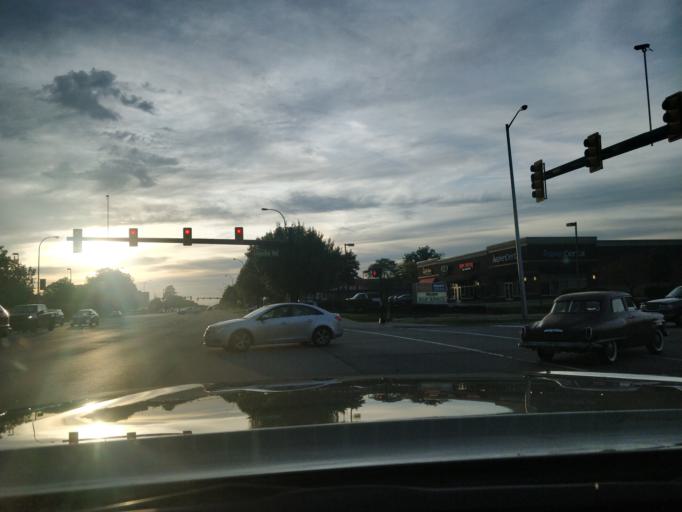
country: US
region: Michigan
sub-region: Wayne County
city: Taylor
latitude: 42.1981
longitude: -83.2478
